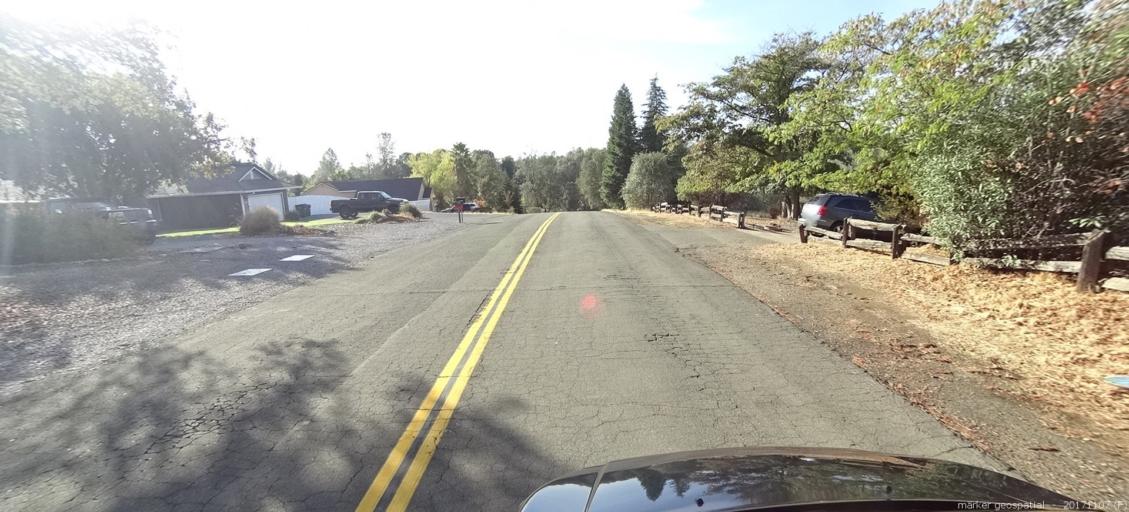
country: US
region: California
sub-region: Shasta County
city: Shasta
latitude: 40.5426
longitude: -122.4572
